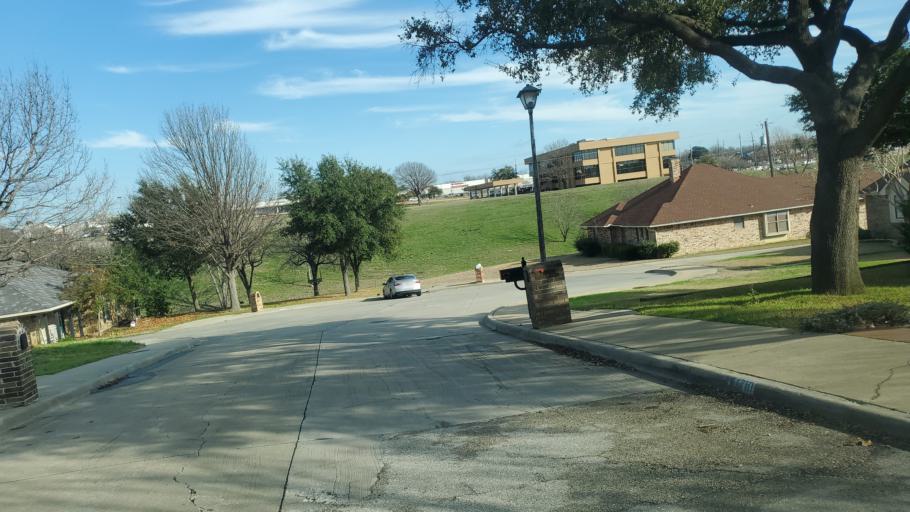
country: US
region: Texas
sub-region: Dallas County
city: Carrollton
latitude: 32.9878
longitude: -96.8935
